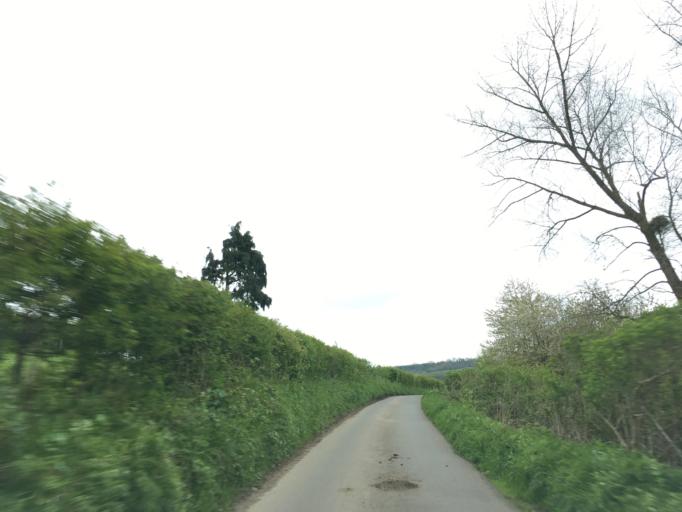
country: GB
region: England
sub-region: Gloucestershire
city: Wotton-under-Edge
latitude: 51.6228
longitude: -2.3282
